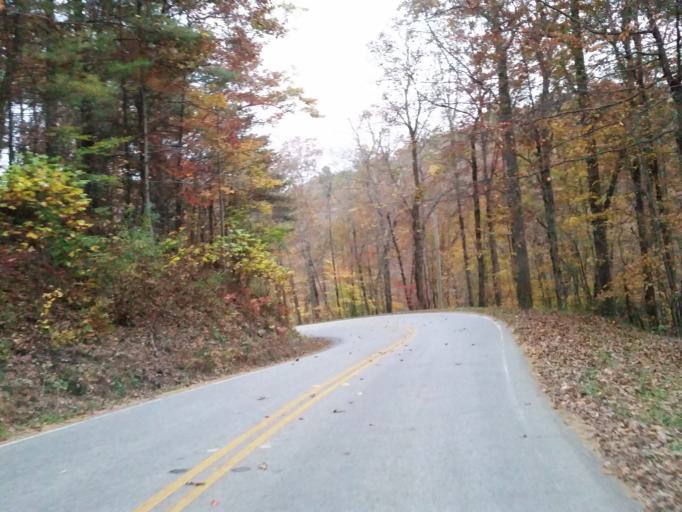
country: US
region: Georgia
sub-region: Lumpkin County
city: Dahlonega
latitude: 34.7050
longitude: -84.0610
